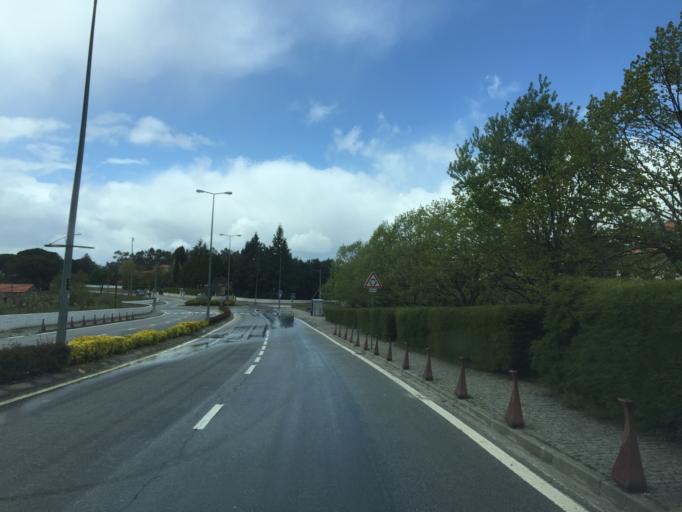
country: PT
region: Guarda
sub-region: Manteigas
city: Manteigas
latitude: 40.5010
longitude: -7.6052
